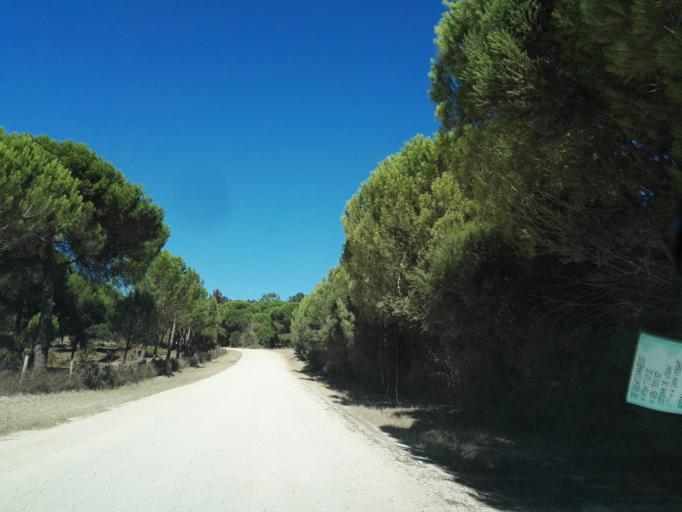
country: PT
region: Santarem
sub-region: Benavente
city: Poceirao
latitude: 38.8722
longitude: -8.7366
